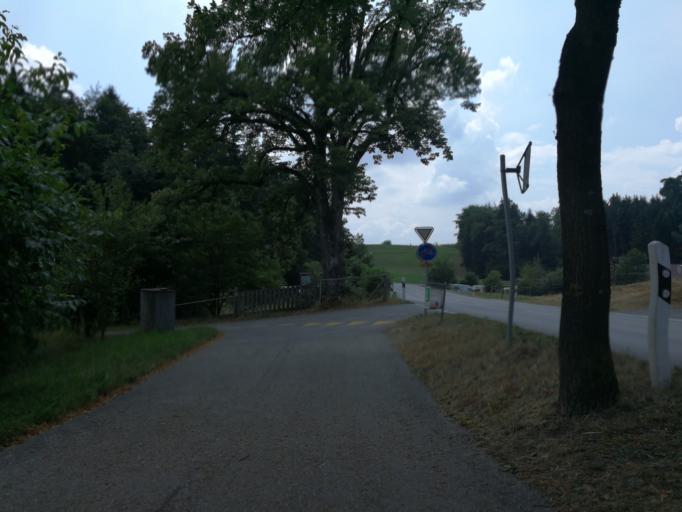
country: CH
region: Zurich
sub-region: Bezirk Hinwil
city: Gossau
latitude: 47.3173
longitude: 8.7570
